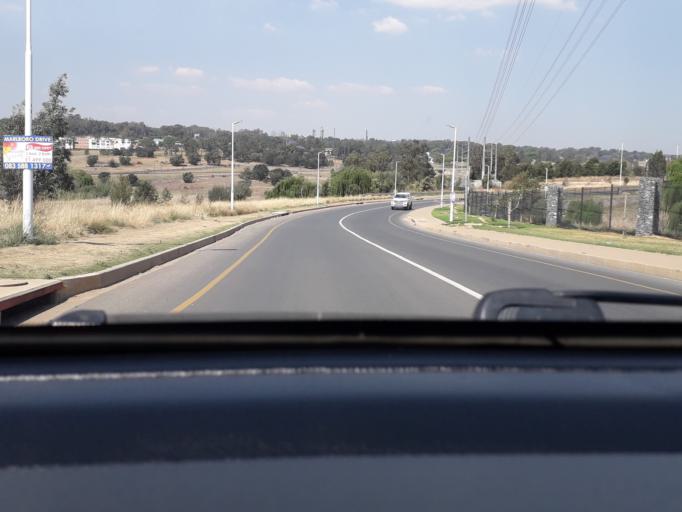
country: ZA
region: Gauteng
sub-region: City of Johannesburg Metropolitan Municipality
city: Modderfontein
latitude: -26.0943
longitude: 28.1433
